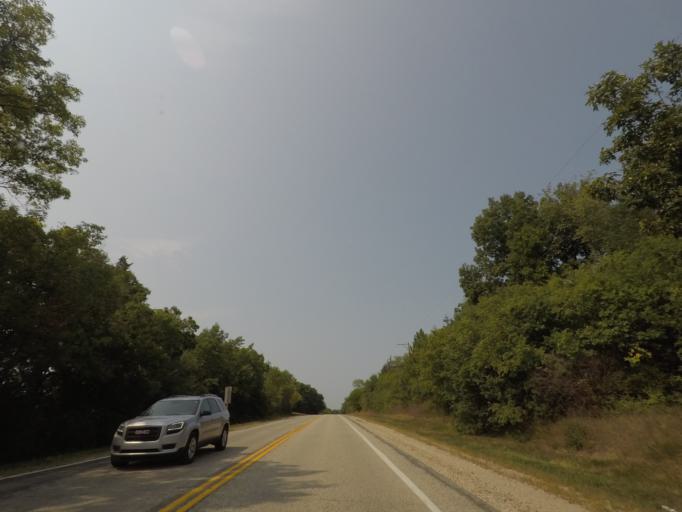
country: US
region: Wisconsin
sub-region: Waukesha County
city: Oconomowoc
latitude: 43.0614
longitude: -88.4975
